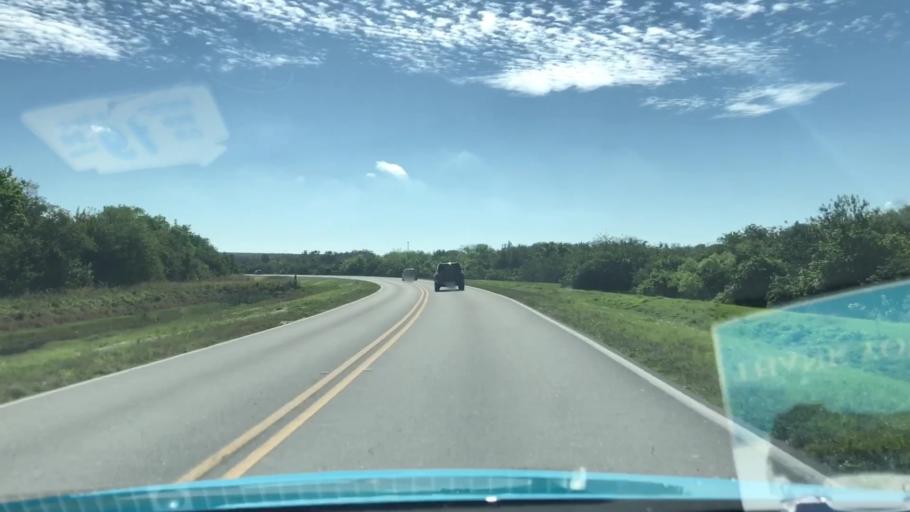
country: US
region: Florida
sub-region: Brevard County
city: Merritt Island
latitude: 28.5165
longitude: -80.6905
